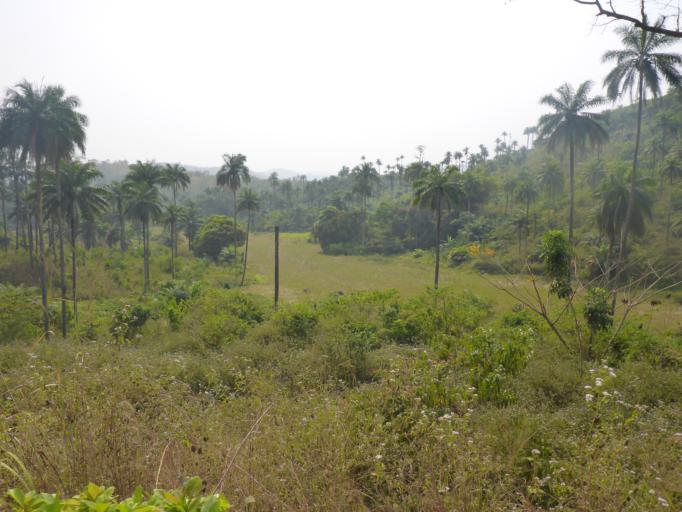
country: SL
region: Northern Province
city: Bumbuna
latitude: 8.9428
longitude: -11.7419
